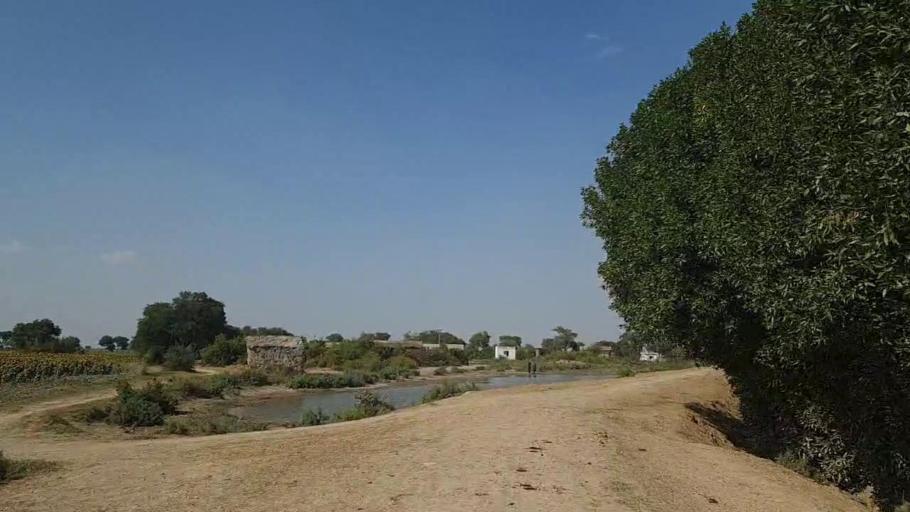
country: PK
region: Sindh
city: Jati
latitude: 24.5199
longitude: 68.2936
